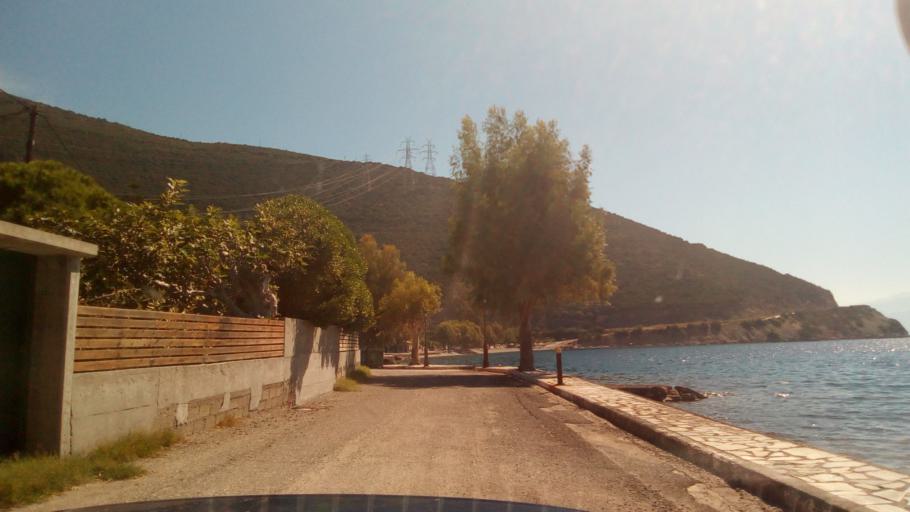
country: GR
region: West Greece
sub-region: Nomos Achaias
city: Aigio
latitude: 38.3671
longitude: 22.1259
